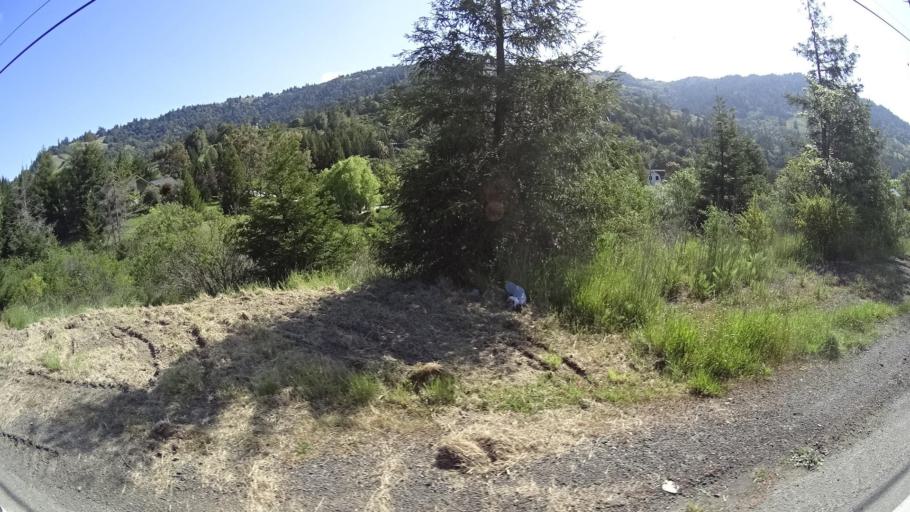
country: US
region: California
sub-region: Humboldt County
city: Redway
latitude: 40.1079
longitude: -123.7851
